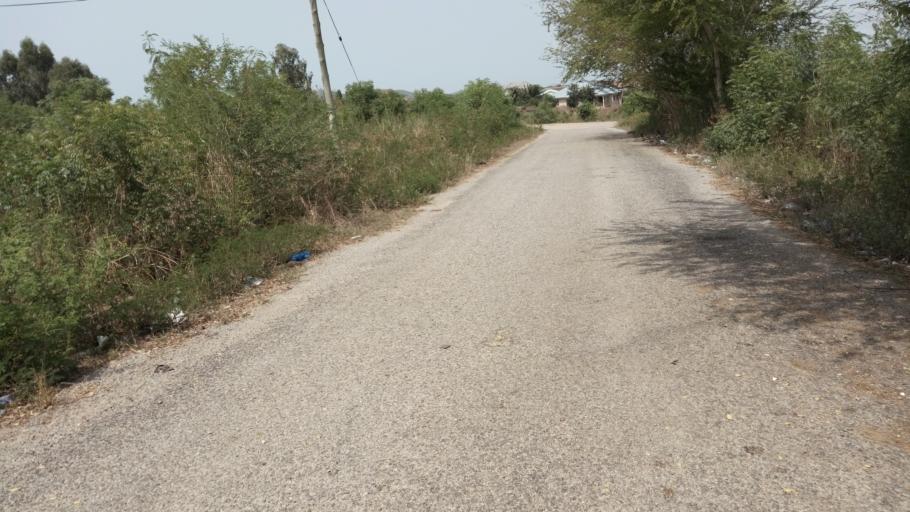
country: GH
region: Central
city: Winneba
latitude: 5.3670
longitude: -0.6462
